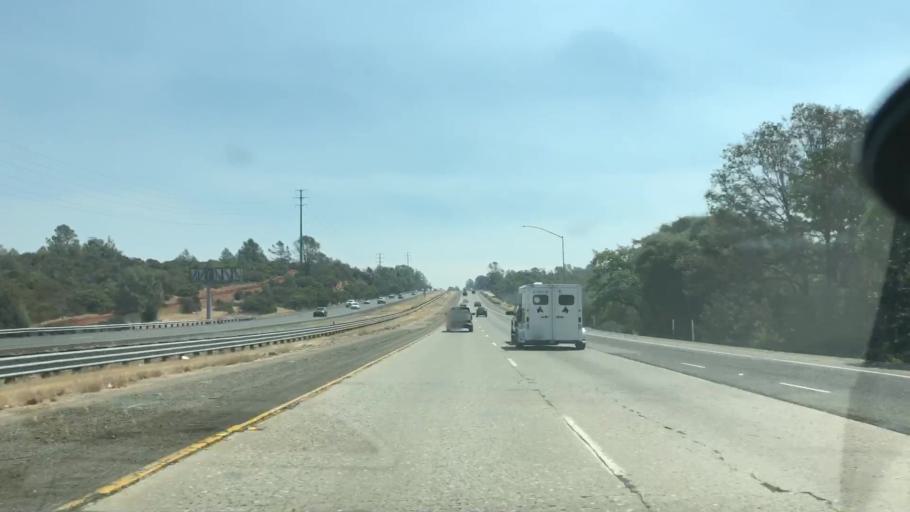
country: US
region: California
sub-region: El Dorado County
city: Cameron Park
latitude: 38.6594
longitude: -120.9655
